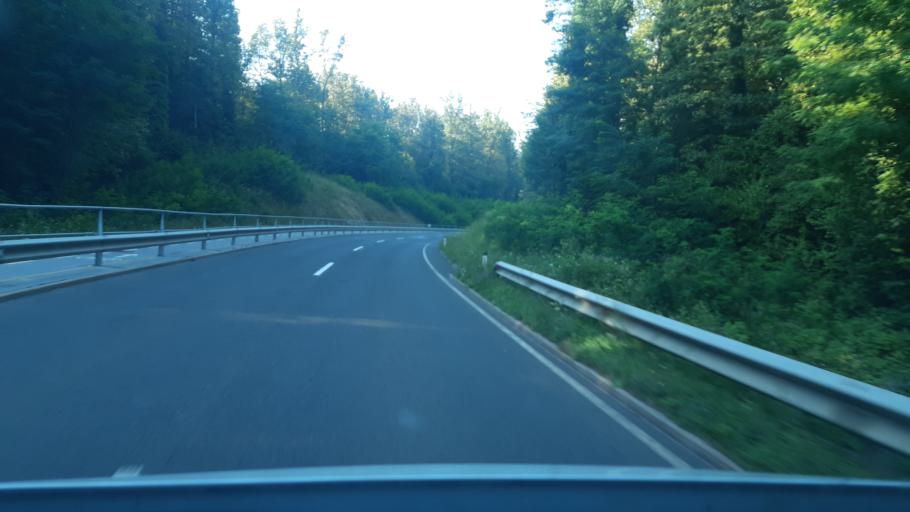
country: SI
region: Crnomelj
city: Crnomelj
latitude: 45.5804
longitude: 15.1812
